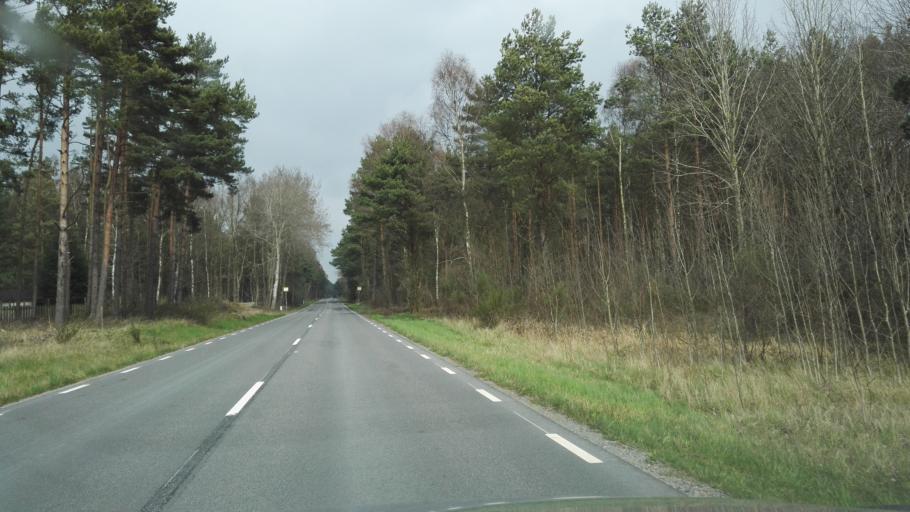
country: SE
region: Skane
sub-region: Simrishamns Kommun
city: Simrishamn
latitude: 55.4010
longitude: 14.1830
